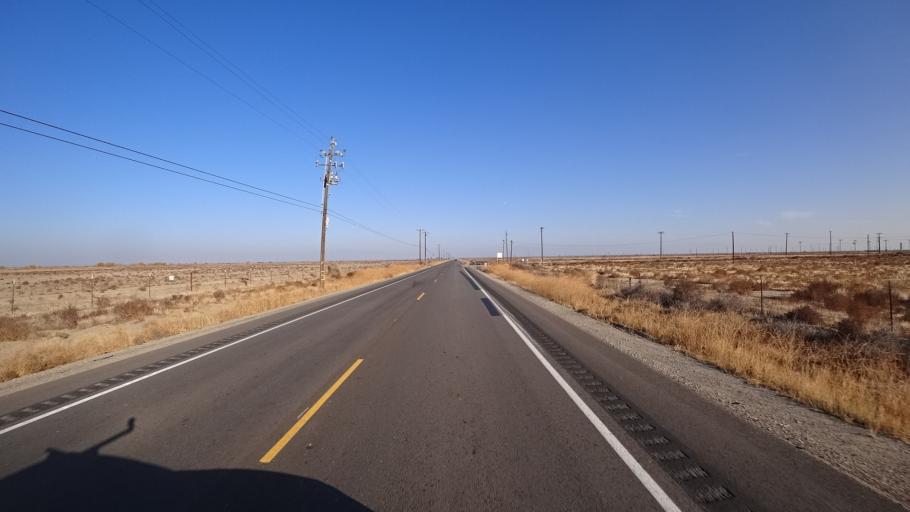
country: US
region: California
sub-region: Kern County
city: Rosedale
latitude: 35.2961
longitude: -119.2160
